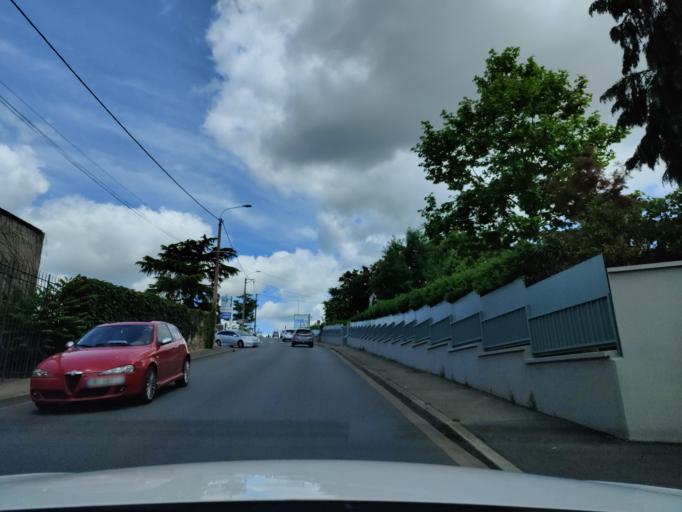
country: FR
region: Auvergne
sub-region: Departement de l'Allier
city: Montlucon
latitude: 46.3420
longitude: 2.6114
